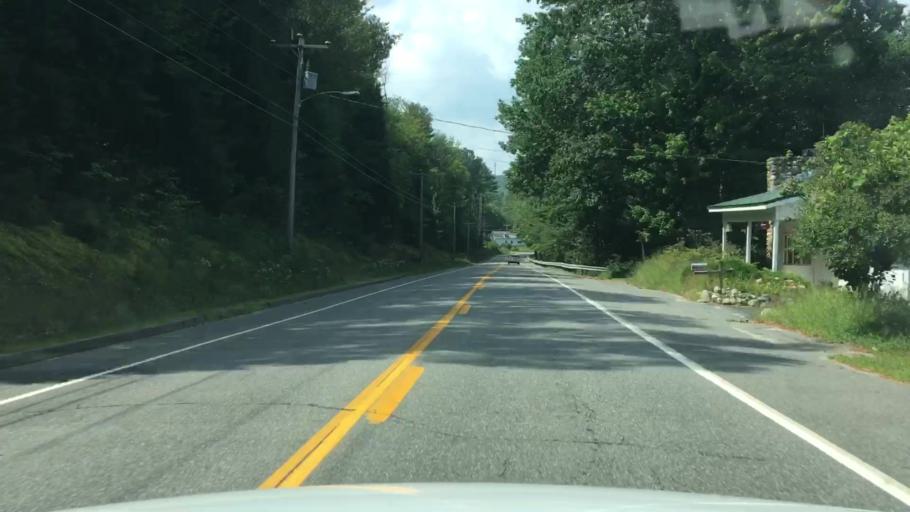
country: US
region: Maine
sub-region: Oxford County
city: Dixfield
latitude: 44.5283
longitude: -70.5037
